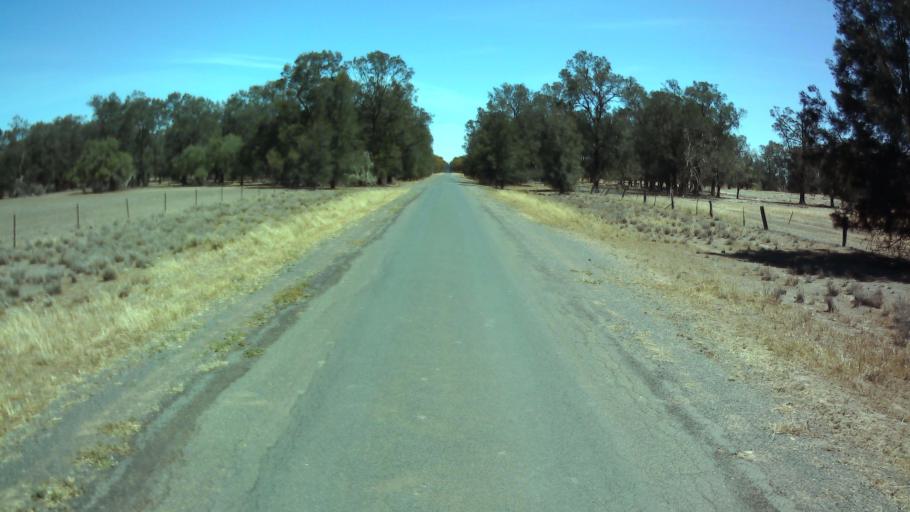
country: AU
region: New South Wales
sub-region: Weddin
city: Grenfell
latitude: -33.8672
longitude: 147.6926
